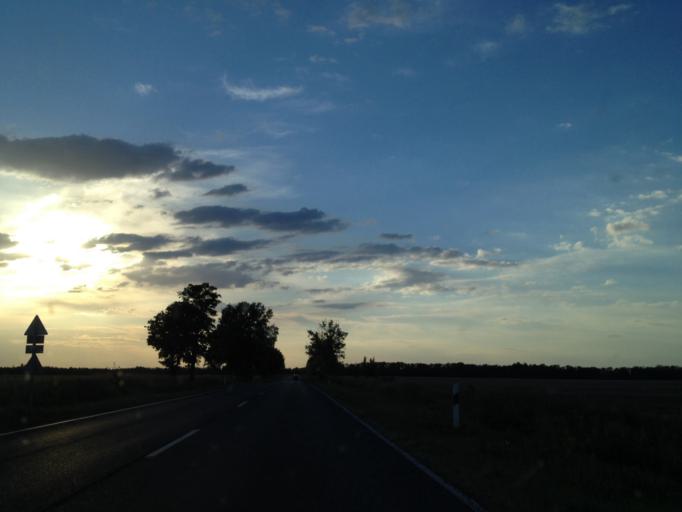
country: HU
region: Gyor-Moson-Sopron
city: Abda
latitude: 47.7109
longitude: 17.5188
